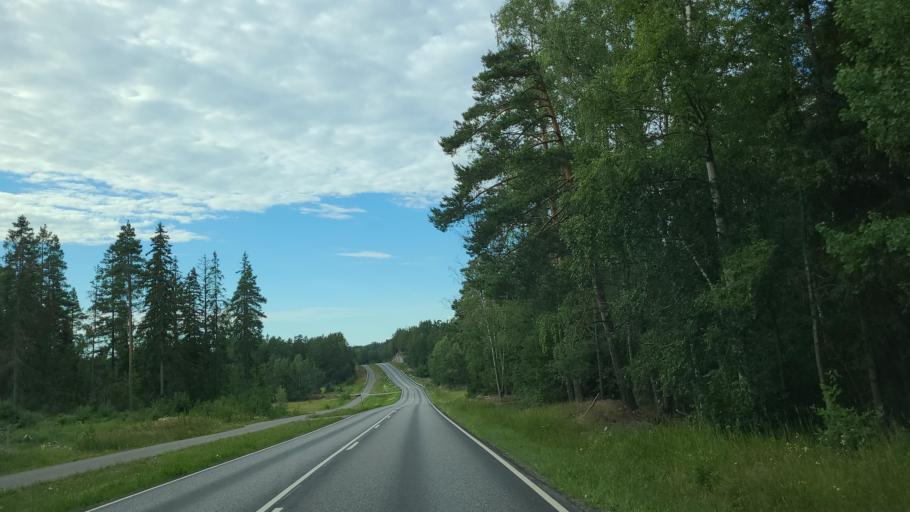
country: FI
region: Varsinais-Suomi
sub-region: Turku
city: Rymaettylae
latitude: 60.3971
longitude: 21.8996
